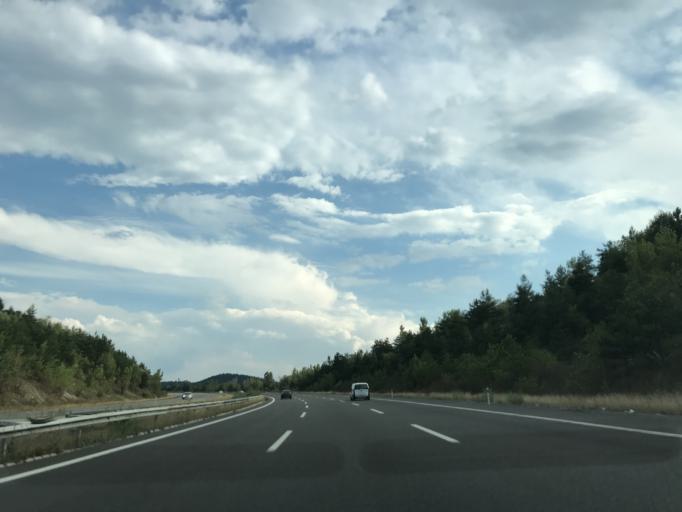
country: TR
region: Bolu
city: Gerede
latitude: 40.6431
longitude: 32.2305
